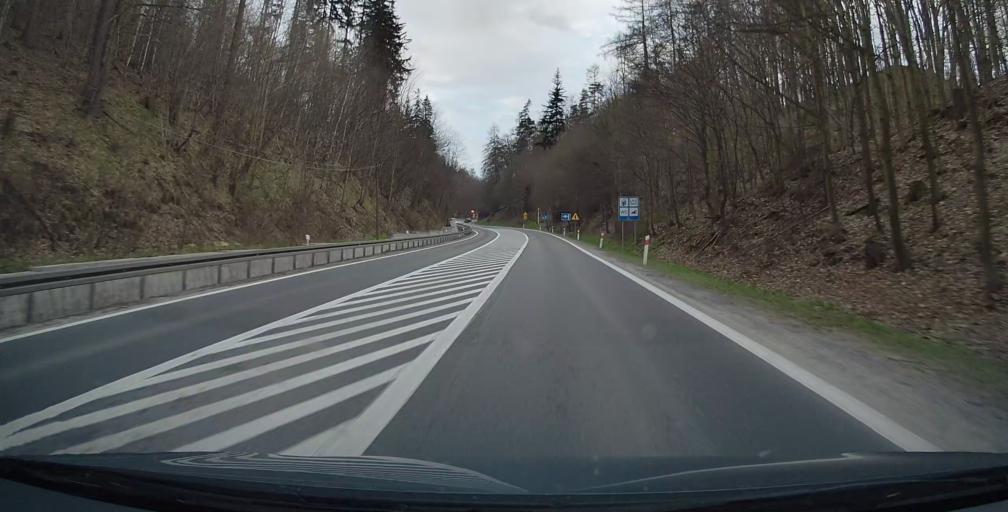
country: PL
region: Lower Silesian Voivodeship
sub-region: Powiat zabkowicki
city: Bardo
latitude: 50.4855
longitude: 16.7132
